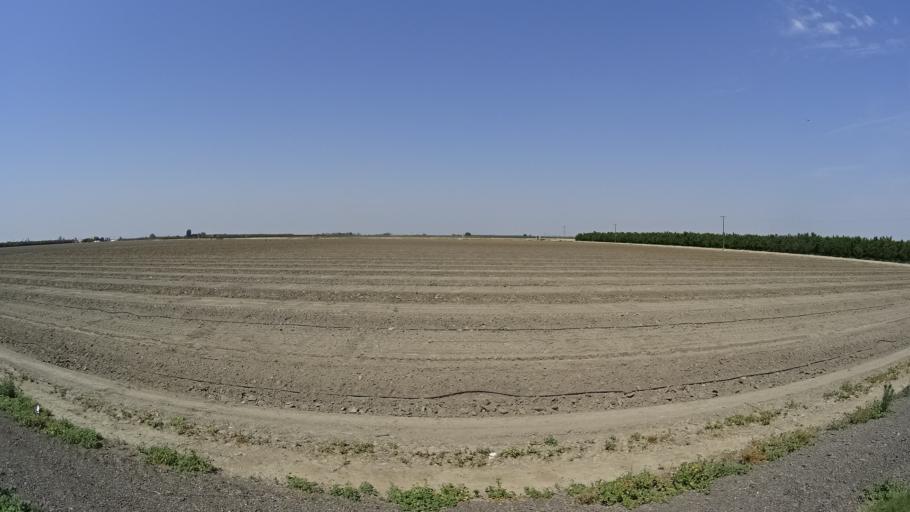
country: US
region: California
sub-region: Kings County
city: Armona
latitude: 36.3493
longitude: -119.7448
